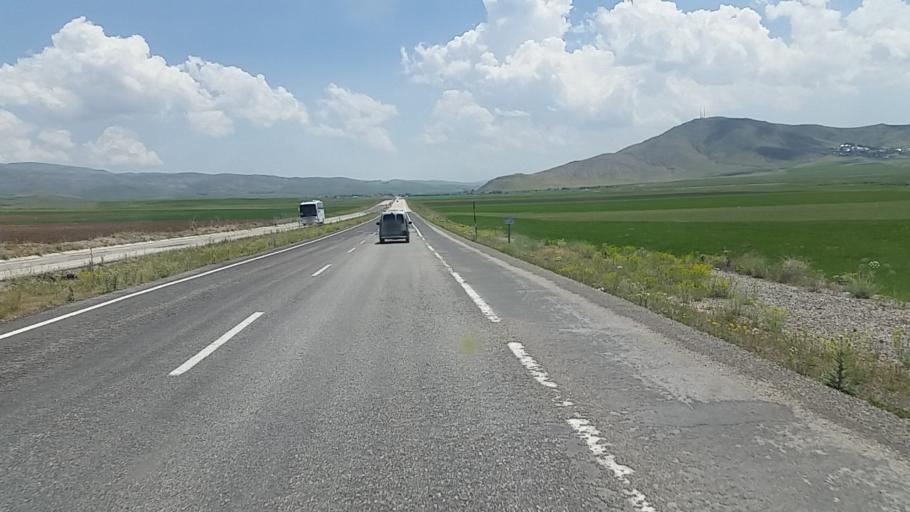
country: TR
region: Agri
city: Taslicay
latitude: 39.6249
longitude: 43.4665
